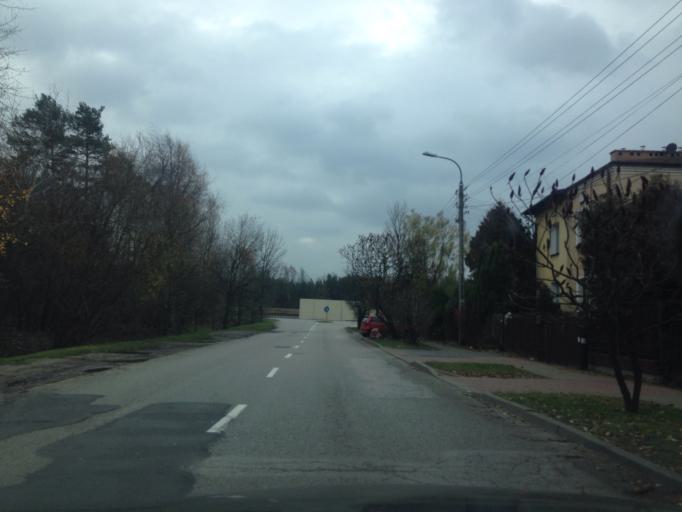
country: PL
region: Masovian Voivodeship
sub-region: Warszawa
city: Rembertow
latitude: 52.2578
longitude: 21.1781
